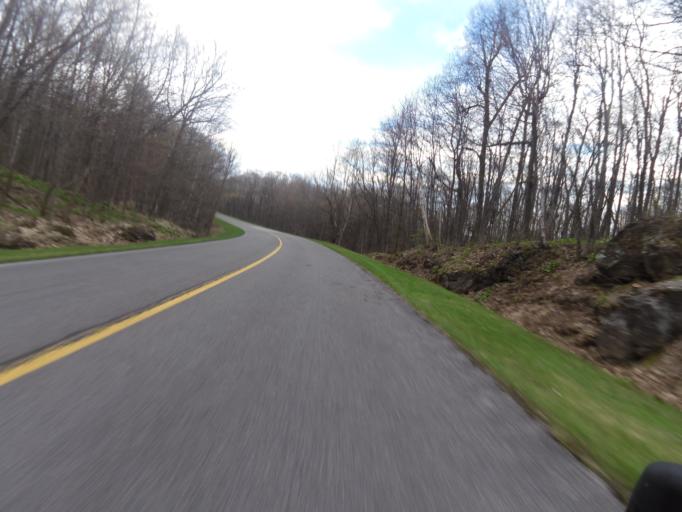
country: CA
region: Quebec
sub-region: Outaouais
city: Gatineau
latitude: 45.4948
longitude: -75.8709
